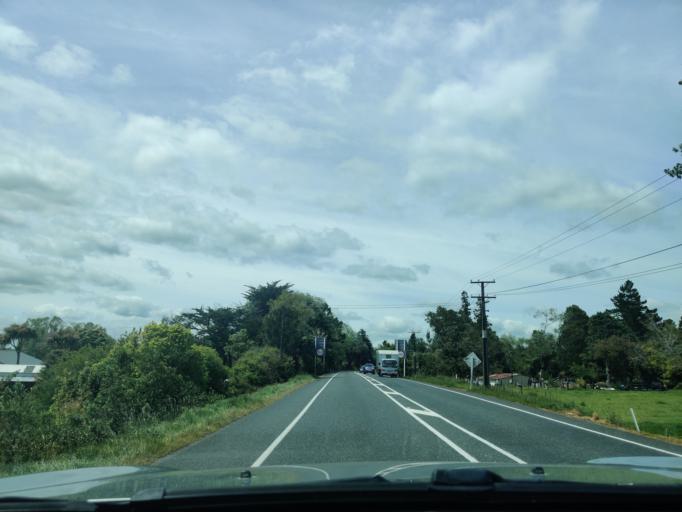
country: NZ
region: Taranaki
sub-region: New Plymouth District
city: New Plymouth
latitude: -39.1466
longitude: 174.1469
